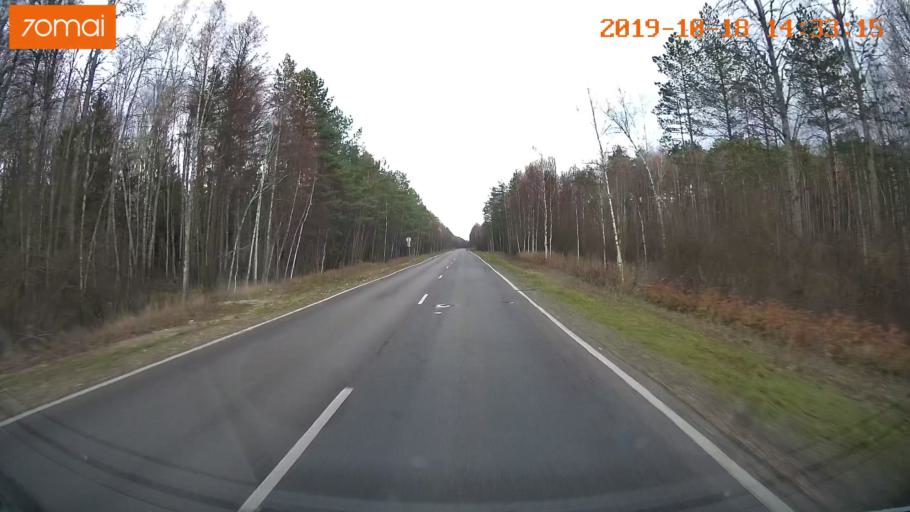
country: RU
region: Rjazan
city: Tuma
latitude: 55.1992
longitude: 40.5933
